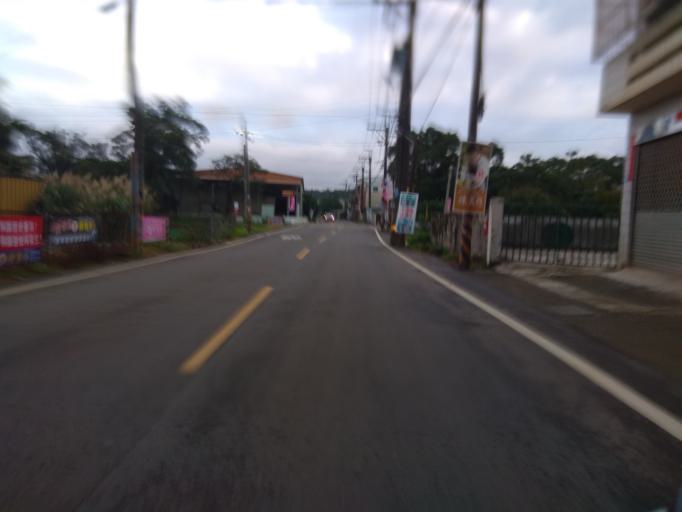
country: TW
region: Taiwan
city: Taoyuan City
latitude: 24.9469
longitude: 121.1888
